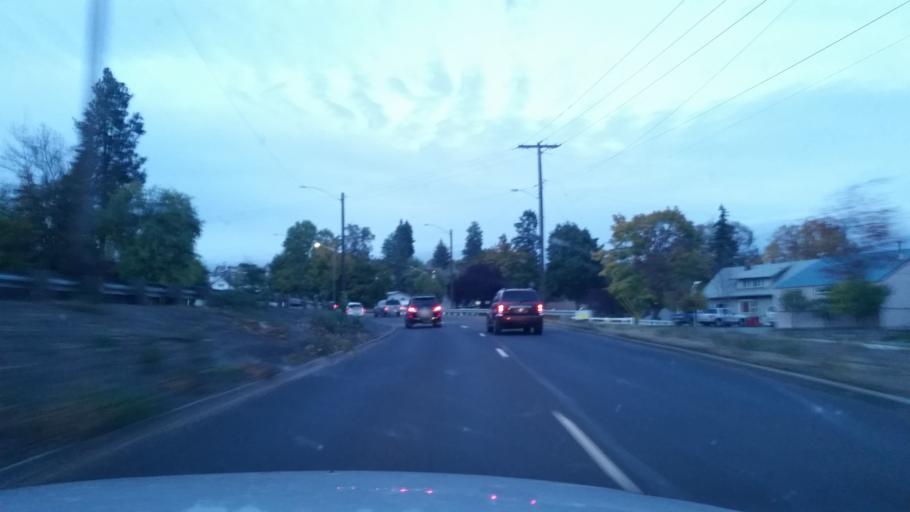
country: US
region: Washington
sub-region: Spokane County
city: Spokane
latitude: 47.6864
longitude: -117.4352
